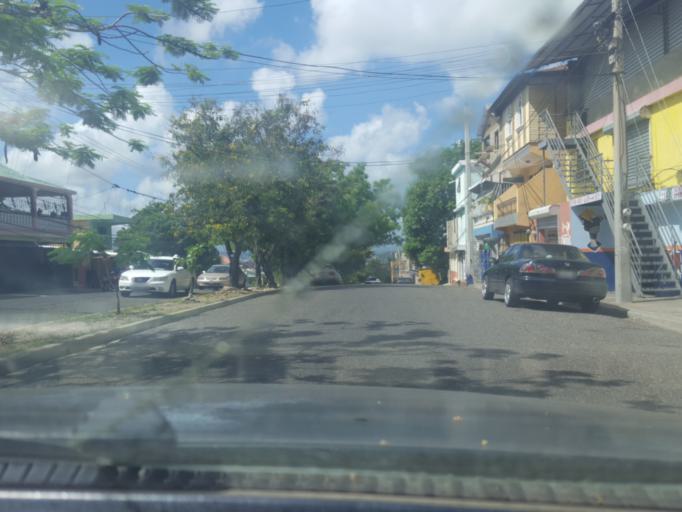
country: DO
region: Santiago
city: Santiago de los Caballeros
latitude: 19.4793
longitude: -70.7057
